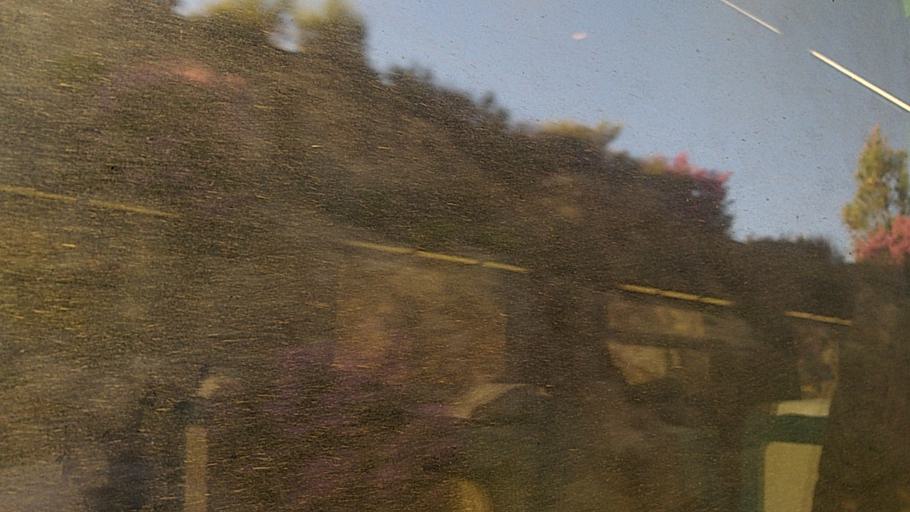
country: PT
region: Guarda
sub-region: Fornos de Algodres
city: Fornos de Algodres
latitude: 40.5941
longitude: -7.5640
